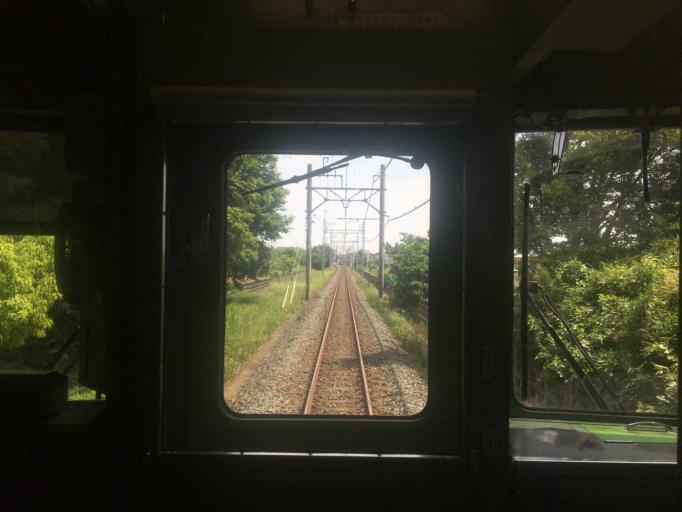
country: JP
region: Saitama
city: Sakado
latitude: 35.9461
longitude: 139.3782
